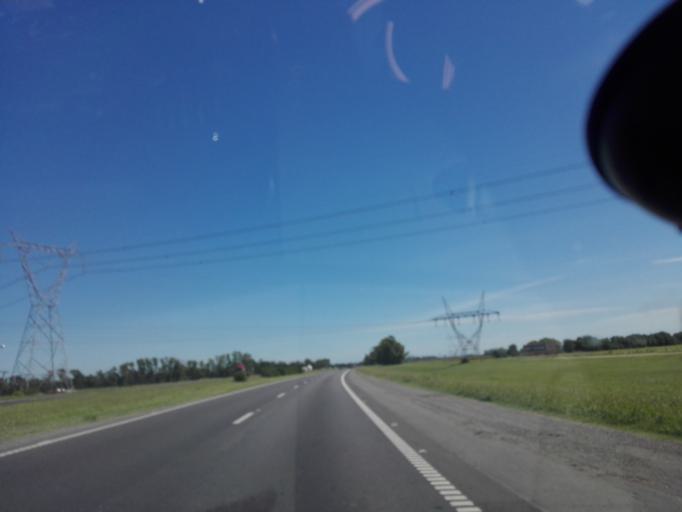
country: AR
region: Buenos Aires
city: San Nicolas de los Arroyos
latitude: -33.4295
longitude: -60.1757
